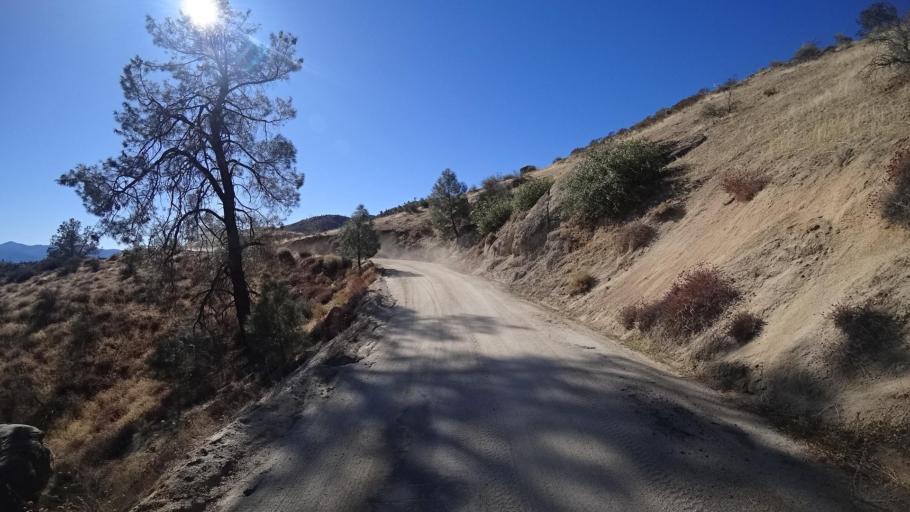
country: US
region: California
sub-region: Kern County
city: Wofford Heights
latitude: 35.7028
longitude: -118.4893
